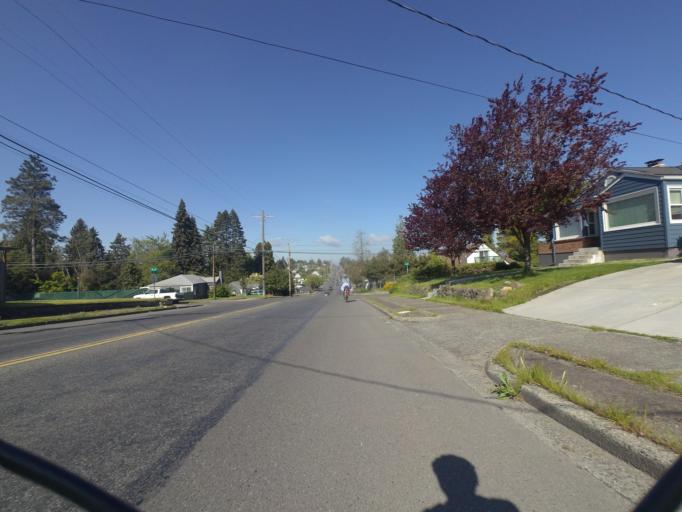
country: US
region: Washington
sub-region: Pierce County
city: Midland
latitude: 47.2065
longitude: -122.4308
